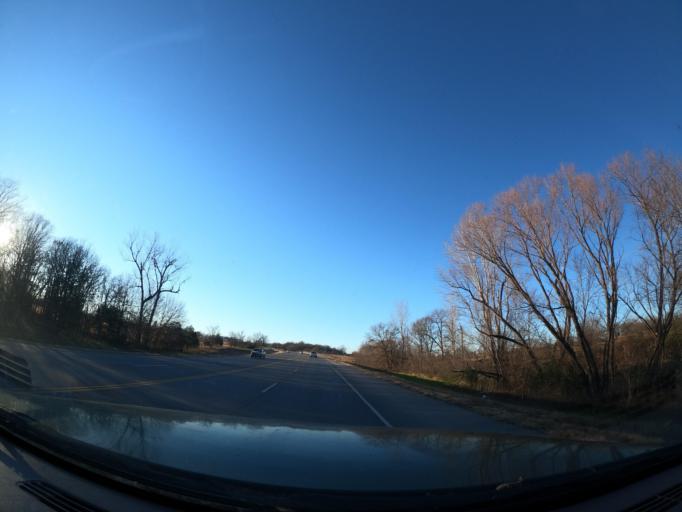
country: US
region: Oklahoma
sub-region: Pittsburg County
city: Hartshorne
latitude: 34.8925
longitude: -95.6234
